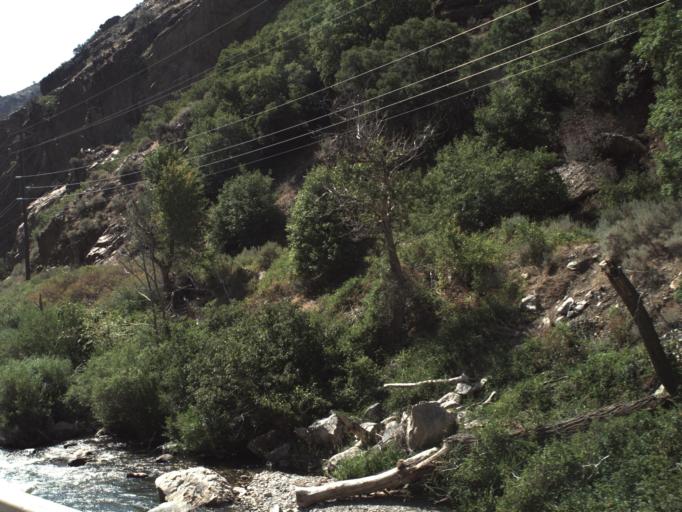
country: US
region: Utah
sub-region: Weber County
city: Ogden
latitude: 41.2380
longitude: -111.9133
